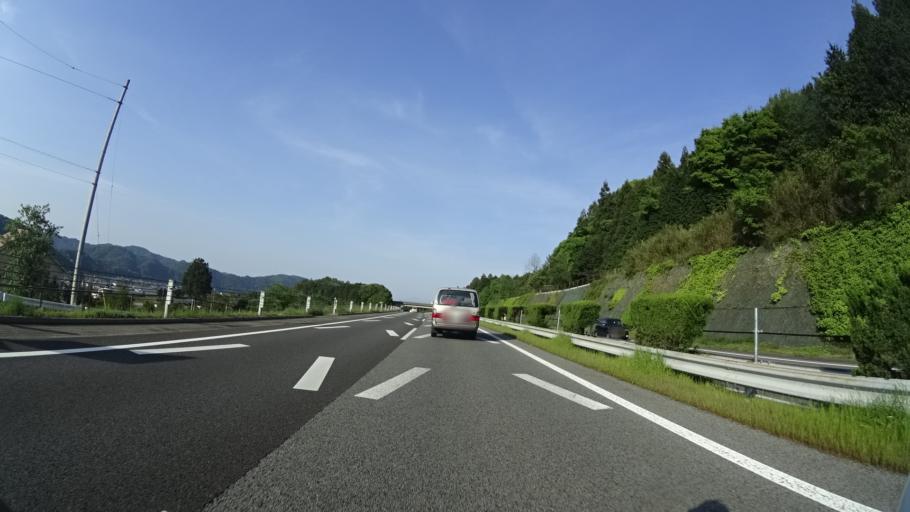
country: JP
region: Ehime
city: Niihama
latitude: 33.9370
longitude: 133.3793
